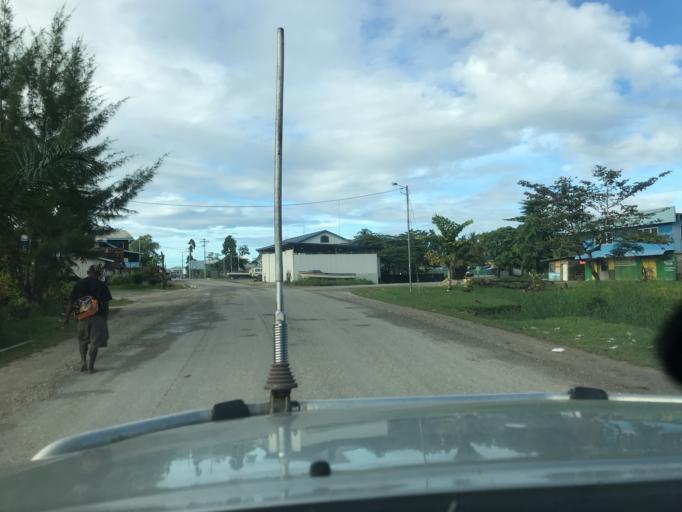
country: SB
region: Malaita
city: Auki
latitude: -8.7690
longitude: 160.6968
